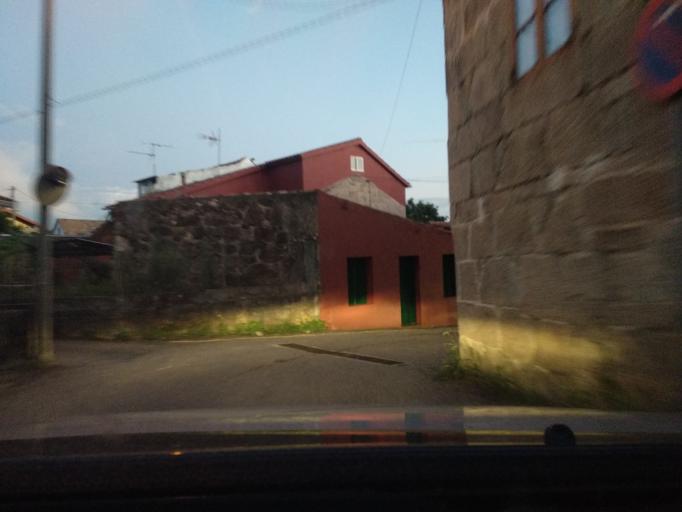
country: ES
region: Galicia
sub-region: Provincia de Pontevedra
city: Moana
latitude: 42.2819
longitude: -8.7465
